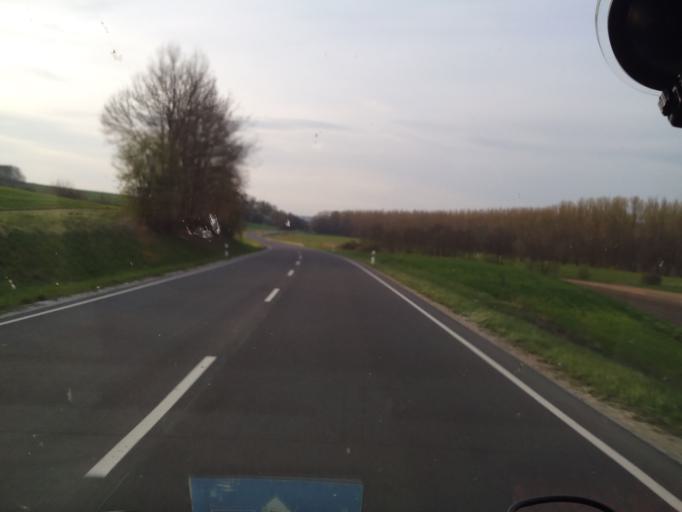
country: DE
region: Bavaria
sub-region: Regierungsbezirk Unterfranken
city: Rentweinsdorf
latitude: 50.0996
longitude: 10.7850
